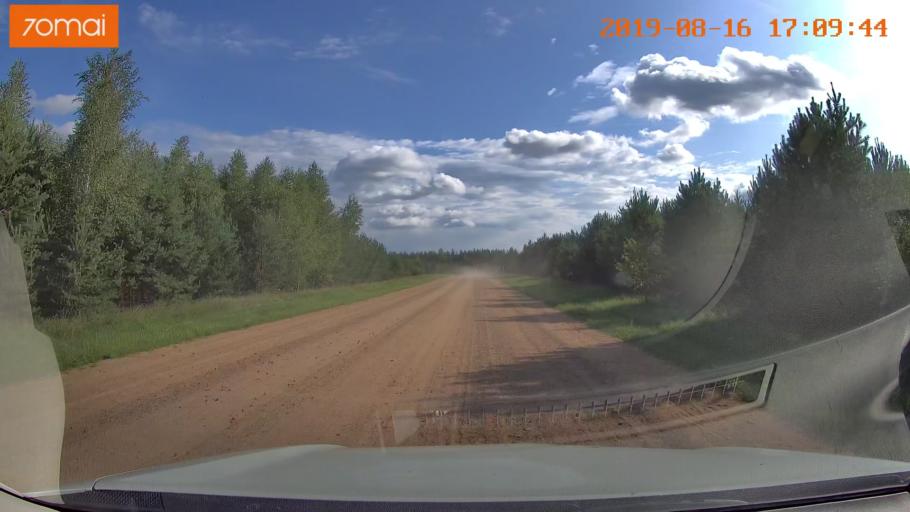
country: BY
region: Mogilev
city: Hlusha
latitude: 53.2094
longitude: 28.9235
